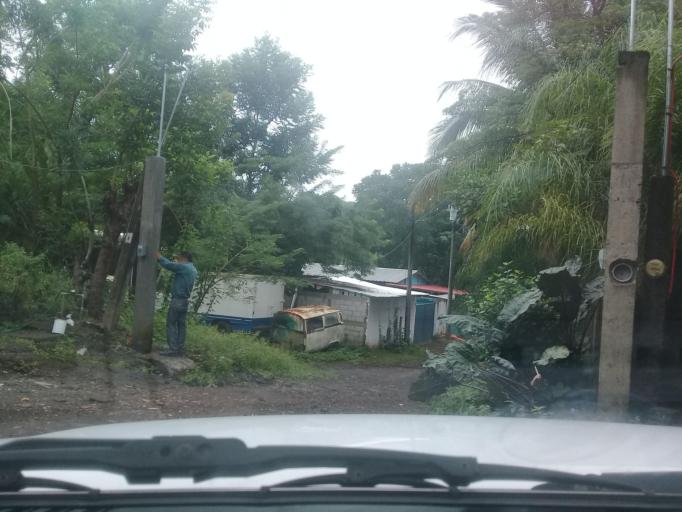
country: MX
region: Veracruz
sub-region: San Andres Tuxtla
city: Cerro las Iguanas
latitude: 18.4301
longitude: -95.1967
